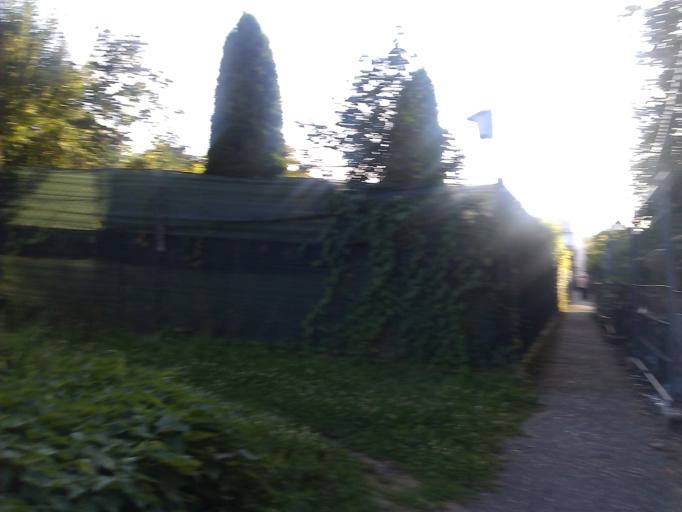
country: DE
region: Baden-Wuerttemberg
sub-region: Karlsruhe Region
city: Rauenberg
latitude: 49.2652
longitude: 8.7074
